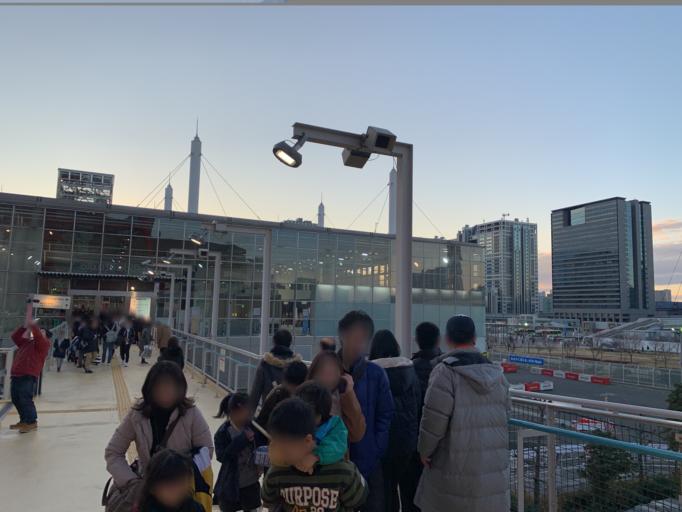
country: JP
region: Tokyo
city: Tokyo
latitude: 35.6264
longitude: 139.7820
